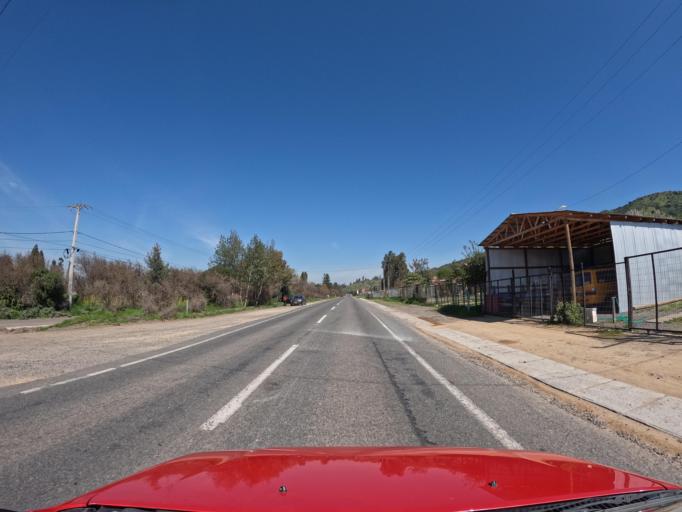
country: CL
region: Maule
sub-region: Provincia de Talca
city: Talca
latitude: -35.0804
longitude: -71.6366
